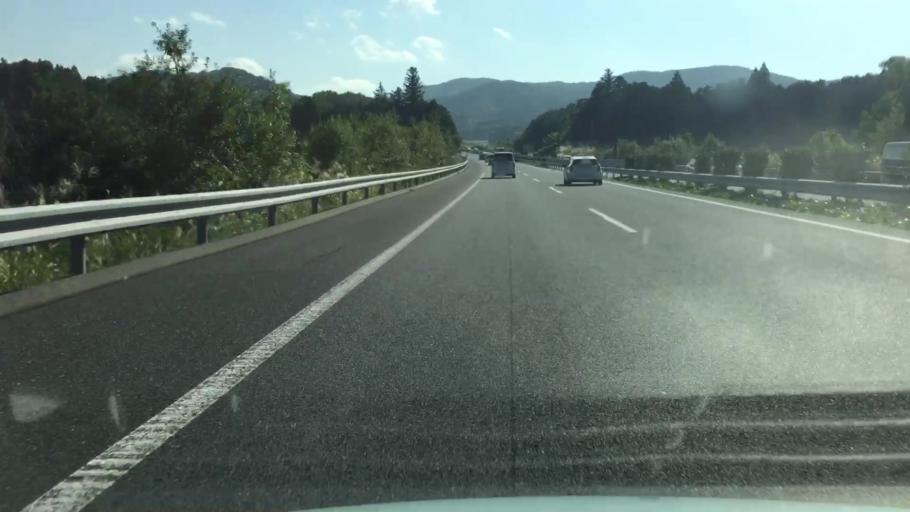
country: JP
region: Ibaraki
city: Iwase
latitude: 36.3443
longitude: 140.1791
